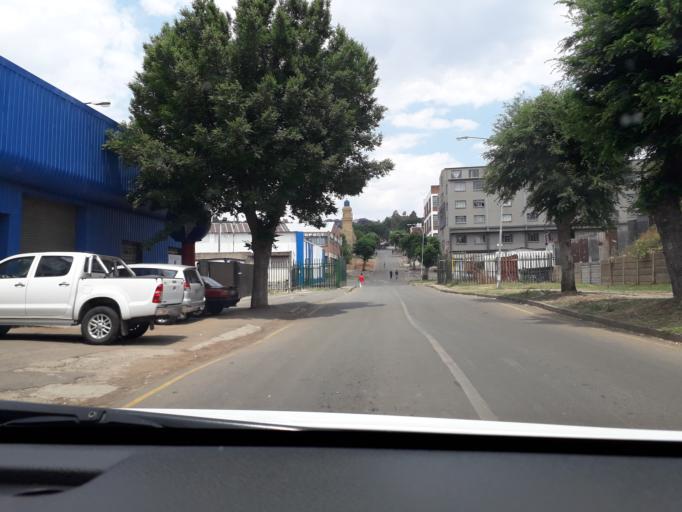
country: ZA
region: Gauteng
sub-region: City of Johannesburg Metropolitan Municipality
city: Johannesburg
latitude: -26.1922
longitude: 28.0731
